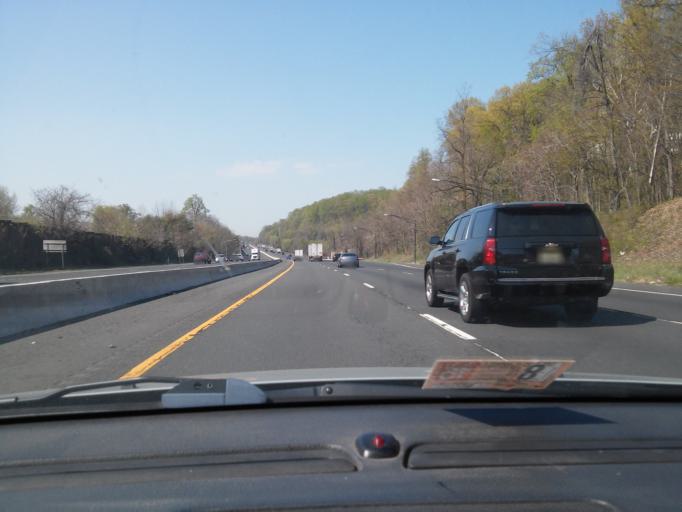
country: US
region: New Jersey
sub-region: Union County
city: New Providence
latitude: 40.6773
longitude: -74.4010
